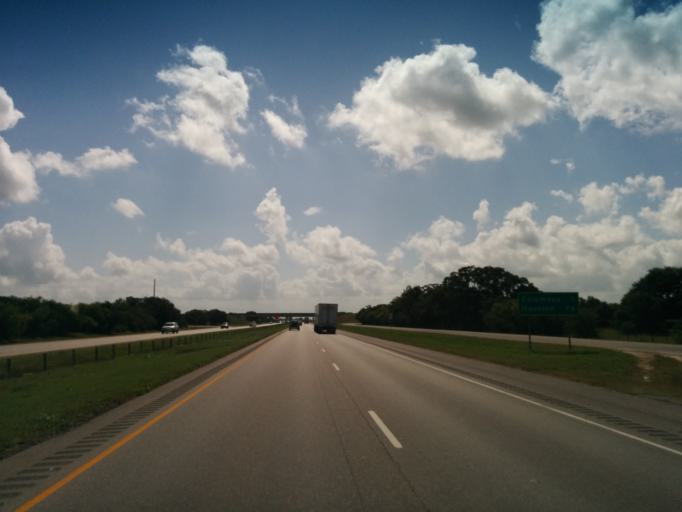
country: US
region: Texas
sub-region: Colorado County
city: Columbus
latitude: 29.6935
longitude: -96.5783
